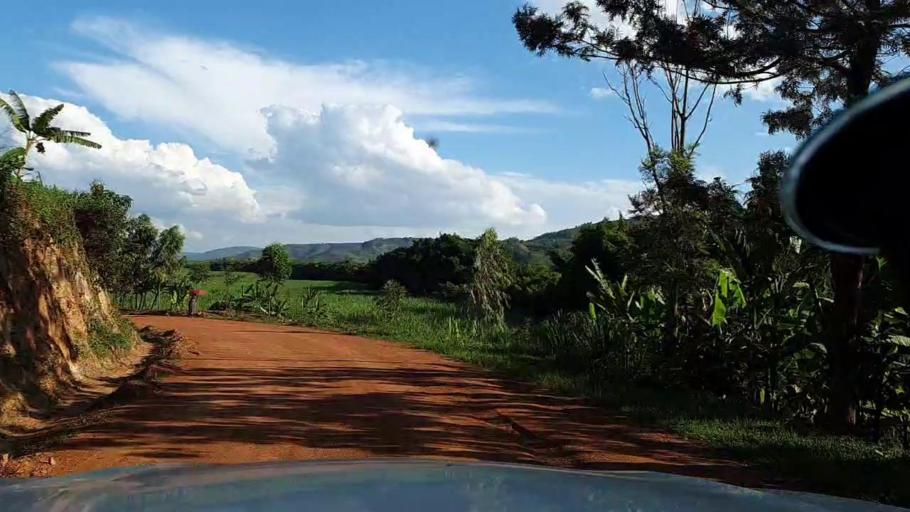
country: RW
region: Kigali
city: Kigali
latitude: -1.8574
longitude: 29.9120
